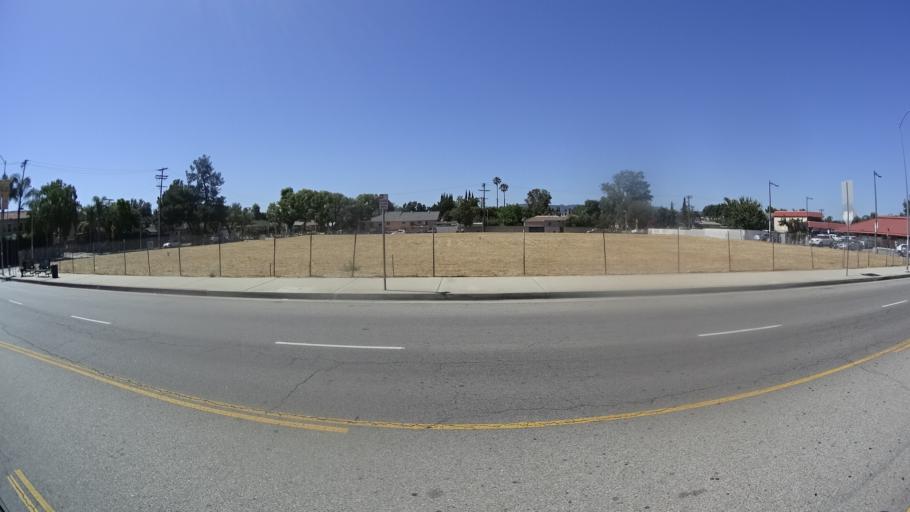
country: US
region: California
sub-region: Los Angeles County
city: Northridge
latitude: 34.1940
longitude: -118.4995
